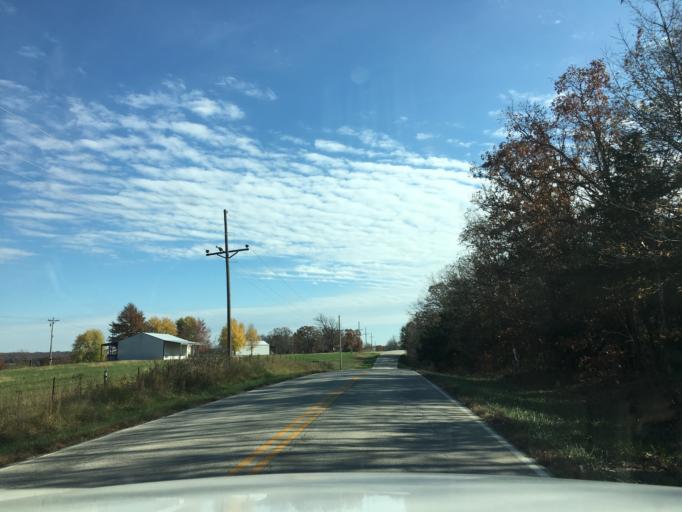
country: US
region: Missouri
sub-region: Maries County
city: Belle
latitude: 38.3570
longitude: -91.8030
